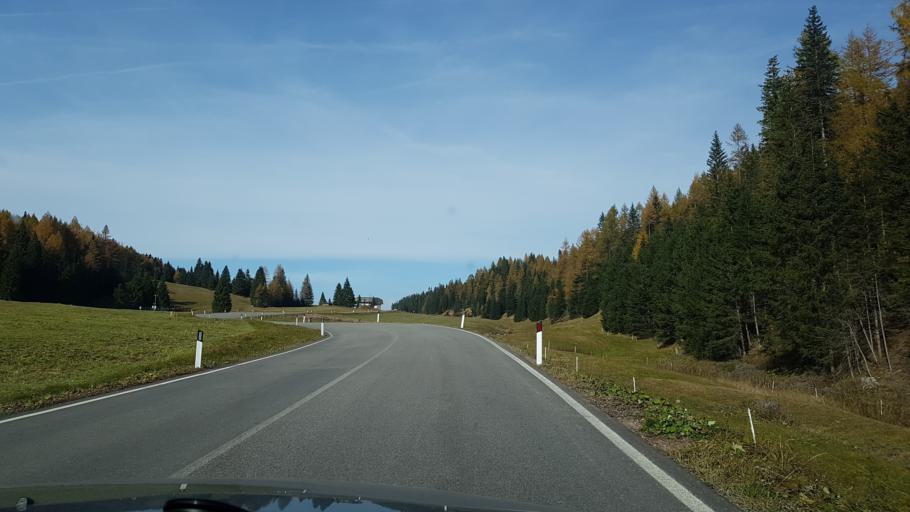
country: IT
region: Veneto
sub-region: Provincia di Belluno
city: Auronzo
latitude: 46.6509
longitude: 12.4268
